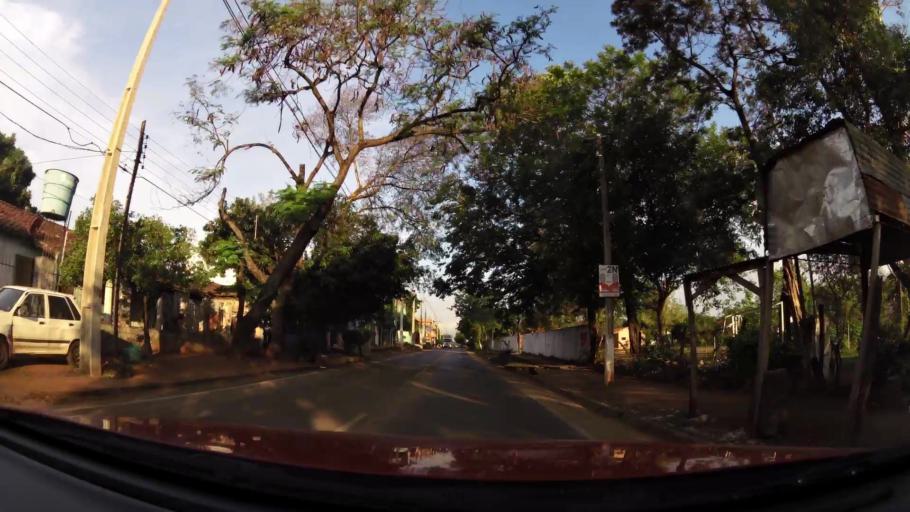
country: PY
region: Central
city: San Lorenzo
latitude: -25.3602
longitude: -57.5078
